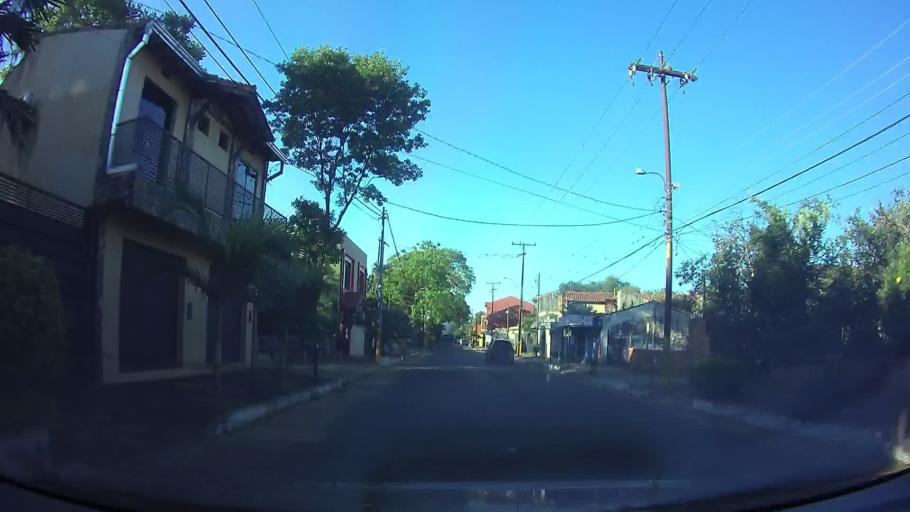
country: PY
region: Central
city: Fernando de la Mora
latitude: -25.3337
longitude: -57.5493
